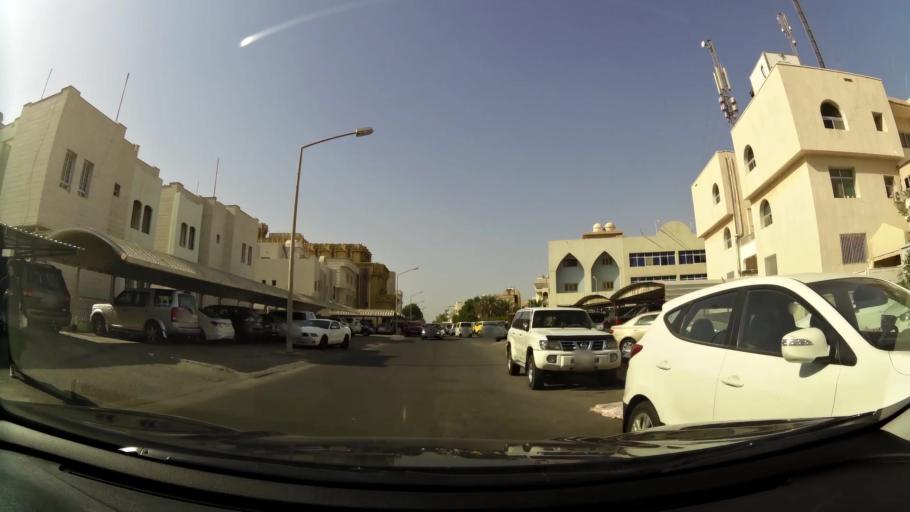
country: KW
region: Muhafazat Hawalli
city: Salwa
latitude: 29.2928
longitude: 48.0717
